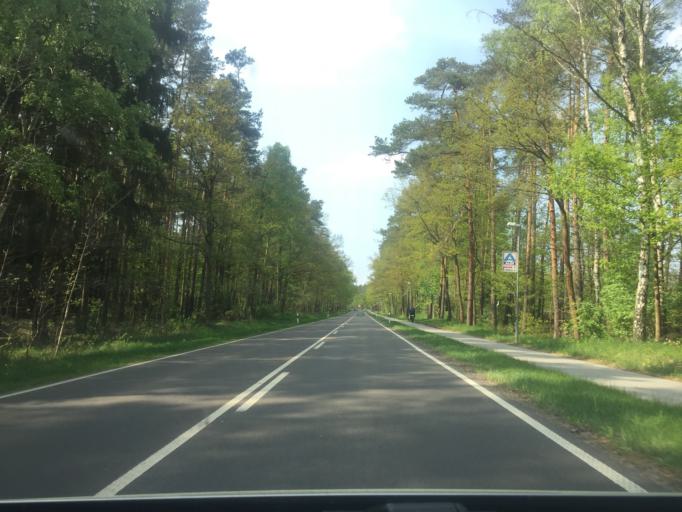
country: DE
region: Mecklenburg-Vorpommern
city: Torgelow
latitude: 53.6174
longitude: 14.0314
